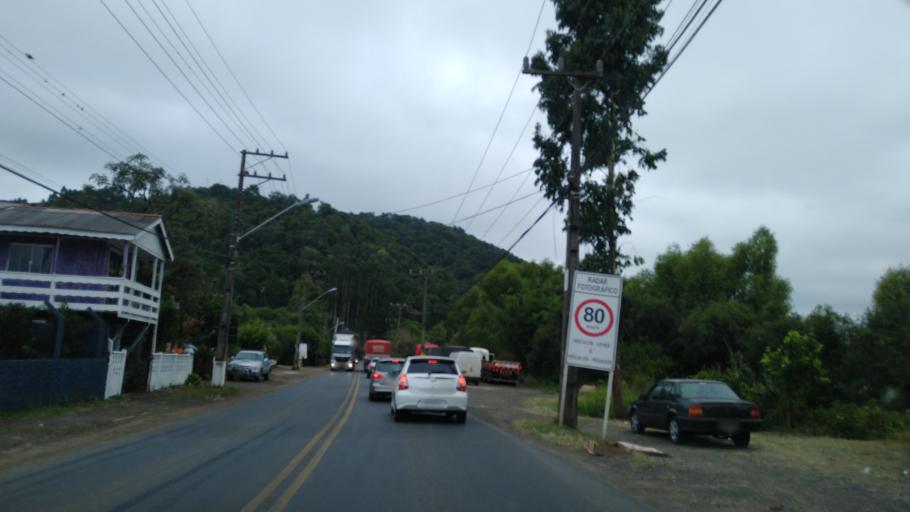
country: BR
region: Parana
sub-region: Uniao Da Vitoria
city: Uniao da Vitoria
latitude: -26.2513
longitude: -51.1014
